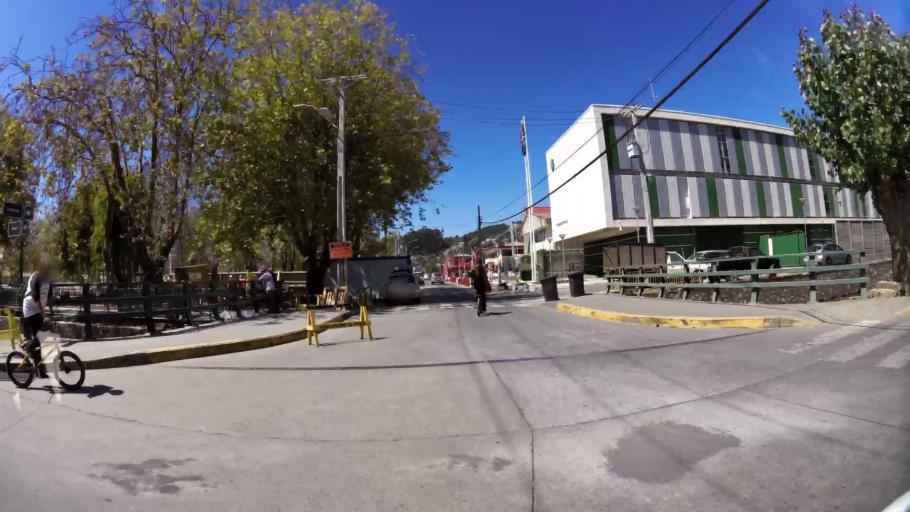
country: CL
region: Biobio
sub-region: Provincia de Concepcion
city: Penco
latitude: -36.7395
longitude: -72.9941
